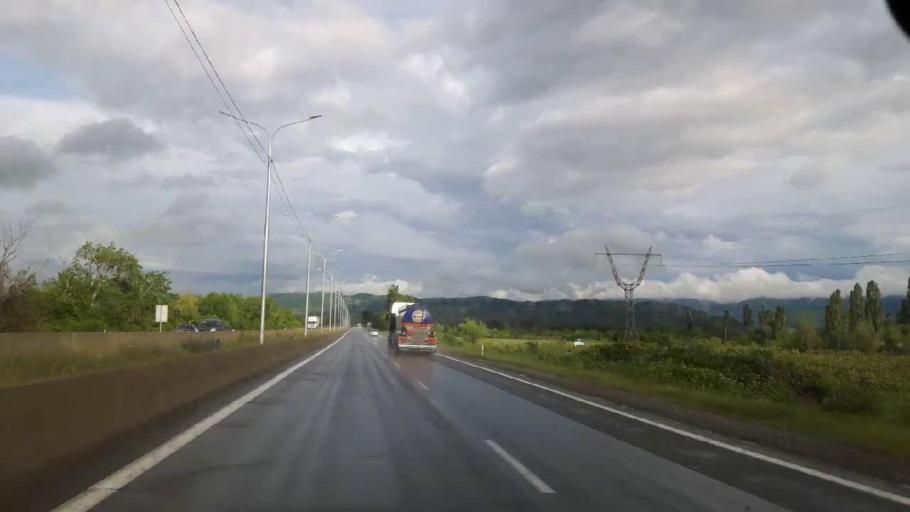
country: GE
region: Shida Kartli
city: Kaspi
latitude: 41.9223
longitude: 44.5449
